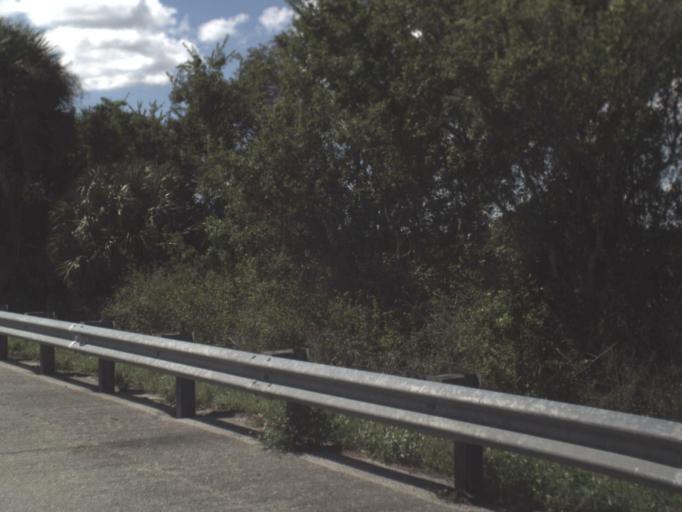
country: US
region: Florida
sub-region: Glades County
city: Buckhead Ridge
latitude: 27.1182
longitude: -80.9249
